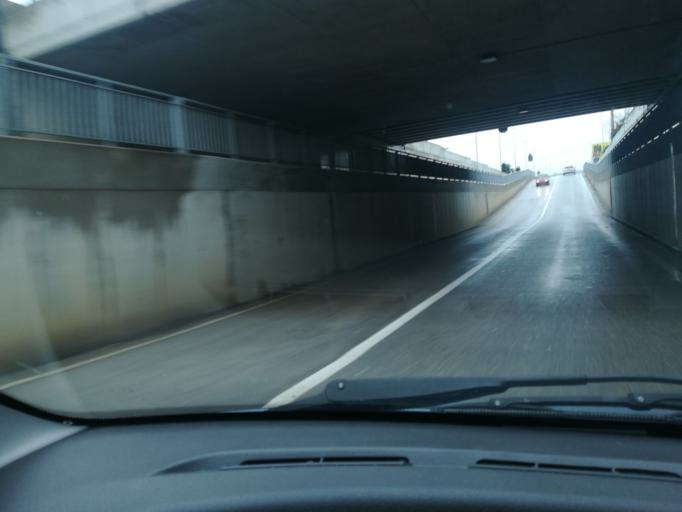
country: IT
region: The Marches
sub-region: Provincia di Macerata
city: Santa Maria Apparente
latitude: 43.2968
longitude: 13.7013
